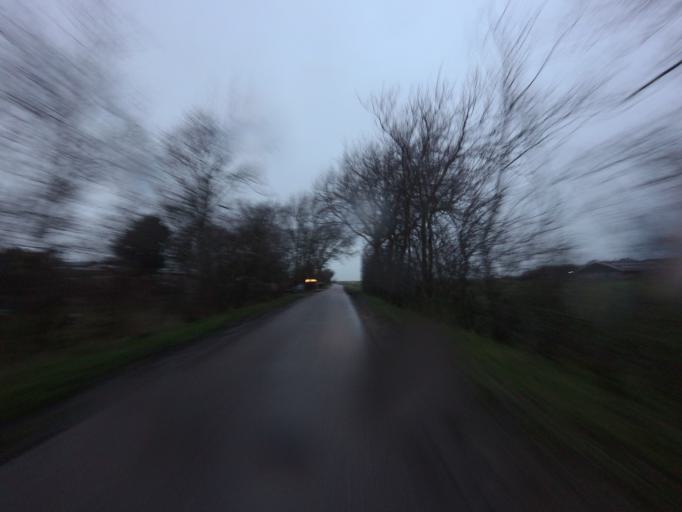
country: NL
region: North Holland
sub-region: Gemeente Texel
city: Den Burg
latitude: 53.0649
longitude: 4.8024
